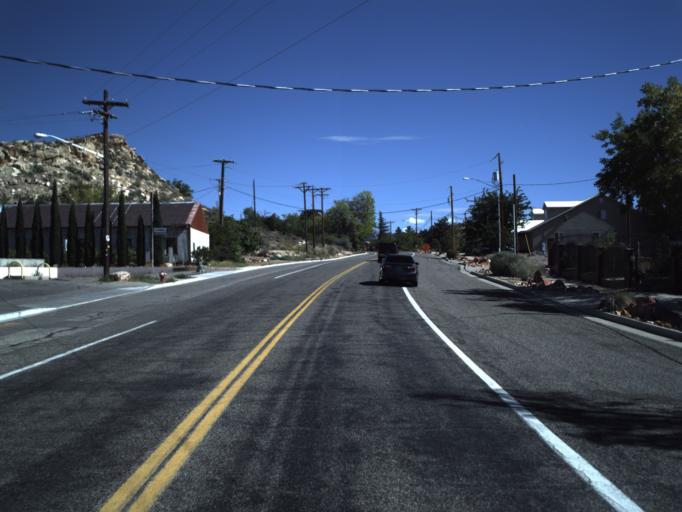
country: US
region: Utah
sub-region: Washington County
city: Toquerville
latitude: 37.2391
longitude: -113.3585
